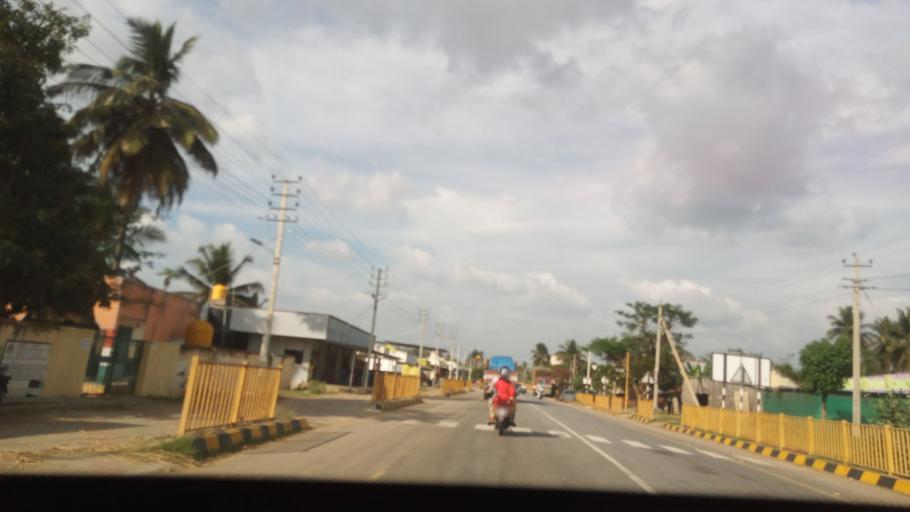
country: IN
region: Karnataka
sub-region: Mandya
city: Maddur
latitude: 12.6653
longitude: 77.0540
